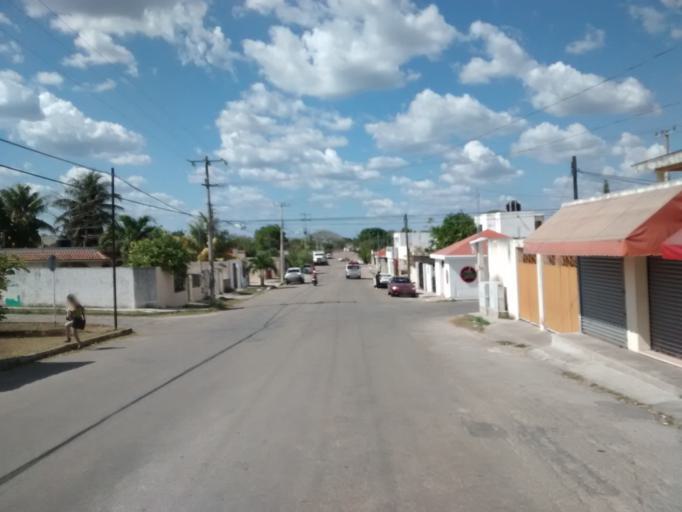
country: MX
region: Yucatan
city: Valladolid
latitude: 20.6962
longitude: -88.2169
